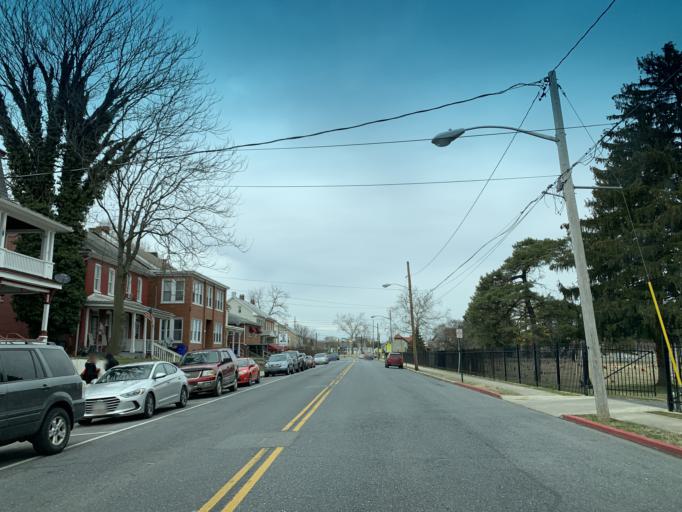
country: US
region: Maryland
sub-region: Washington County
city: Hagerstown
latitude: 39.6306
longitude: -77.7241
